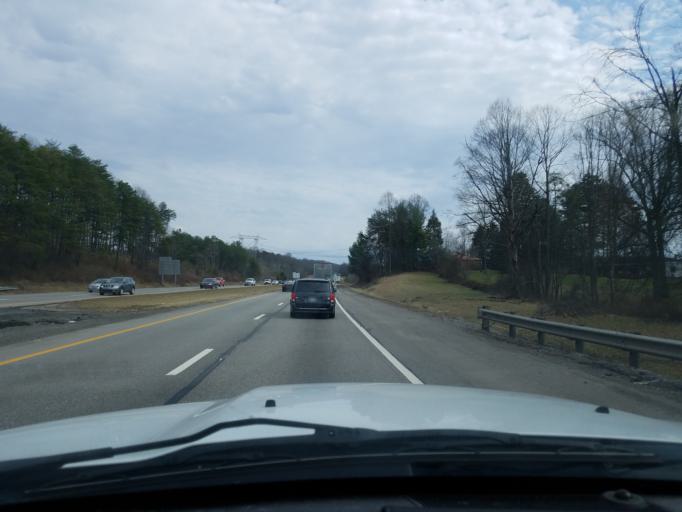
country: US
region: West Virginia
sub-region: Putnam County
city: Teays Valley
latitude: 38.4556
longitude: -81.8817
